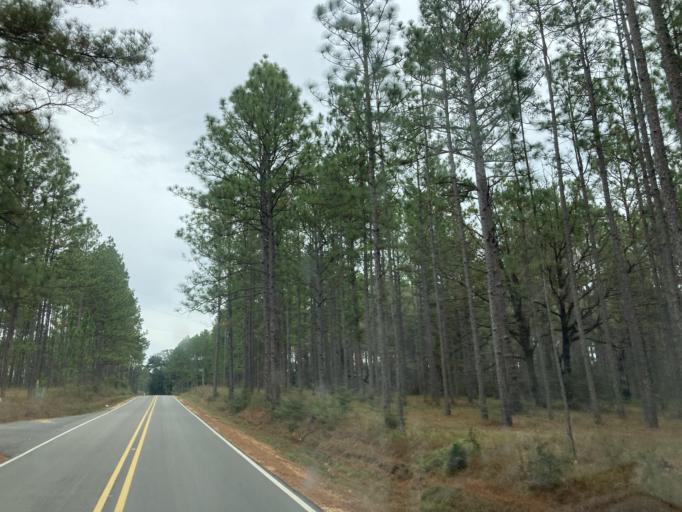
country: US
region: Mississippi
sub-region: Lamar County
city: Purvis
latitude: 31.1093
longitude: -89.4295
